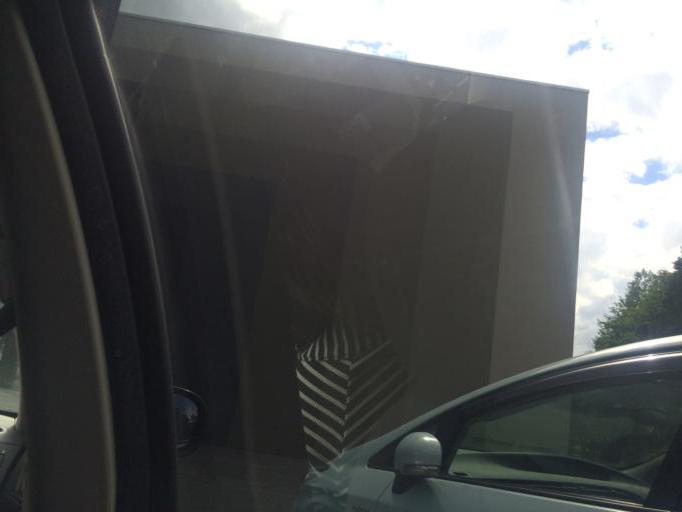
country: JP
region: Hokkaido
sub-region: Asahikawa-shi
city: Asahikawa
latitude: 43.7687
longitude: 142.2866
